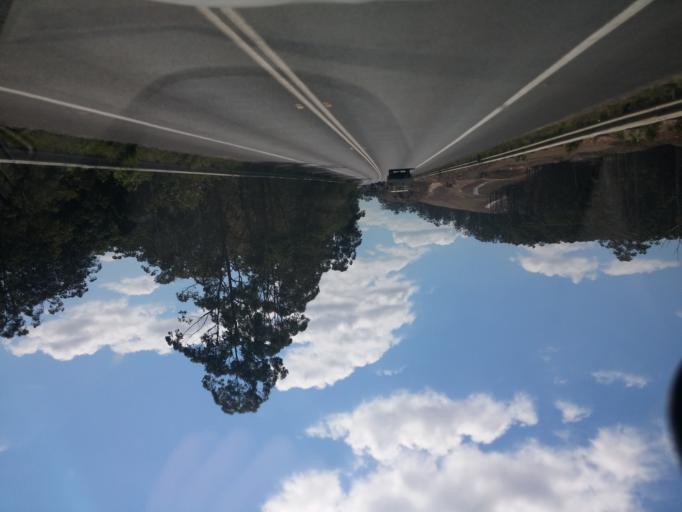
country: AU
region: New South Wales
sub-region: Port Macquarie-Hastings
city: North Shore
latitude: -31.2718
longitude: 152.8124
